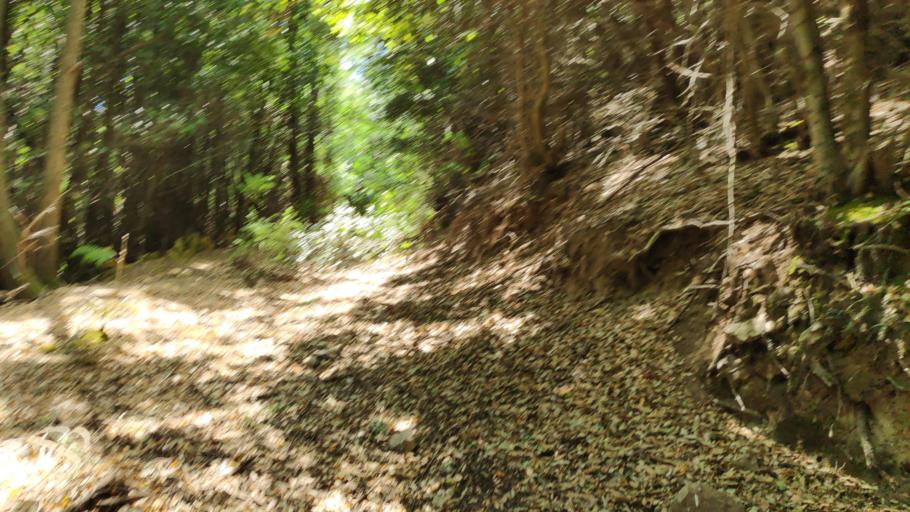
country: IT
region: Calabria
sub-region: Provincia di Reggio Calabria
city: Pazzano
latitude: 38.4782
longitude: 16.4161
